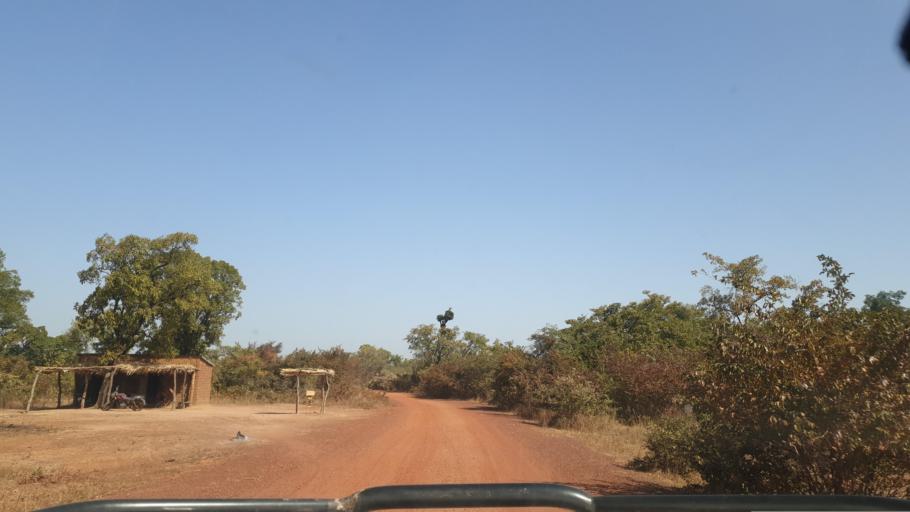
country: ML
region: Sikasso
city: Bougouni
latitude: 11.8294
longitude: -6.9789
